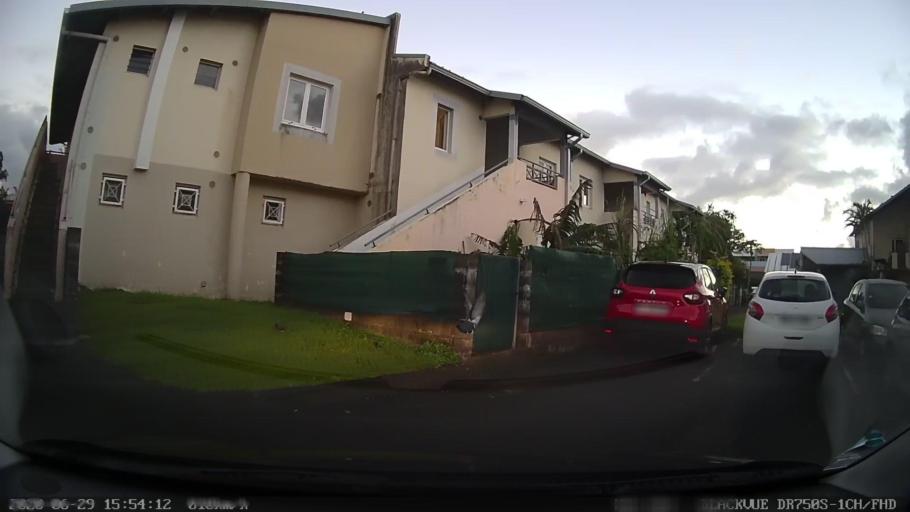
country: RE
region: Reunion
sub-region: Reunion
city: Bras-Panon
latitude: -21.0005
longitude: 55.6943
